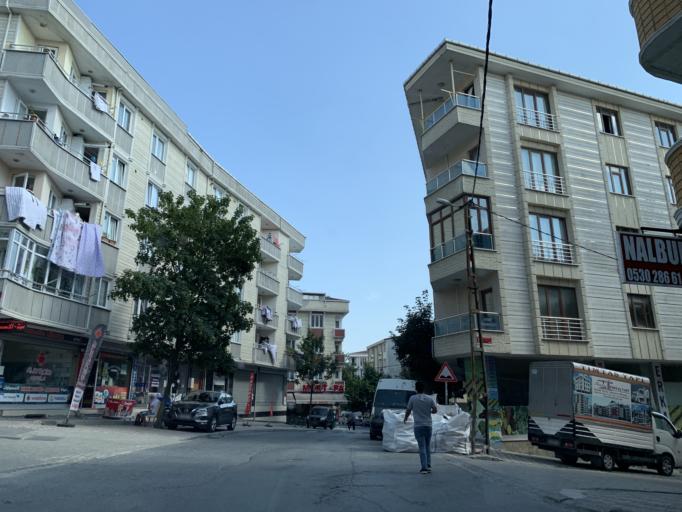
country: TR
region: Istanbul
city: Esenyurt
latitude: 41.0381
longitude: 28.6751
